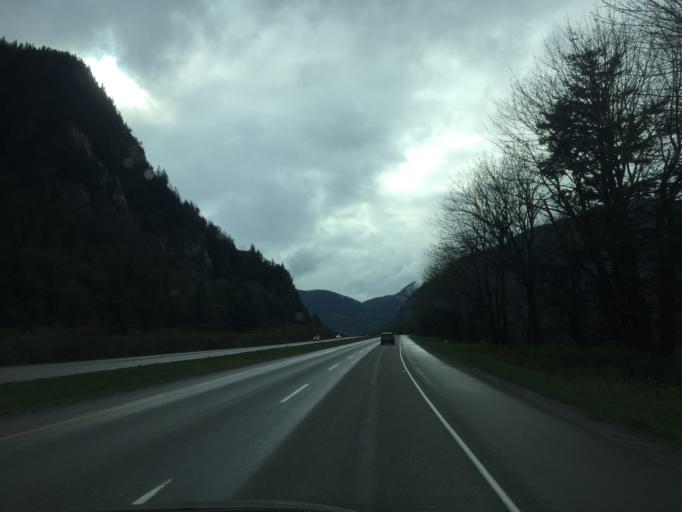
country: CA
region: British Columbia
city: Hope
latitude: 49.3634
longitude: -121.5528
